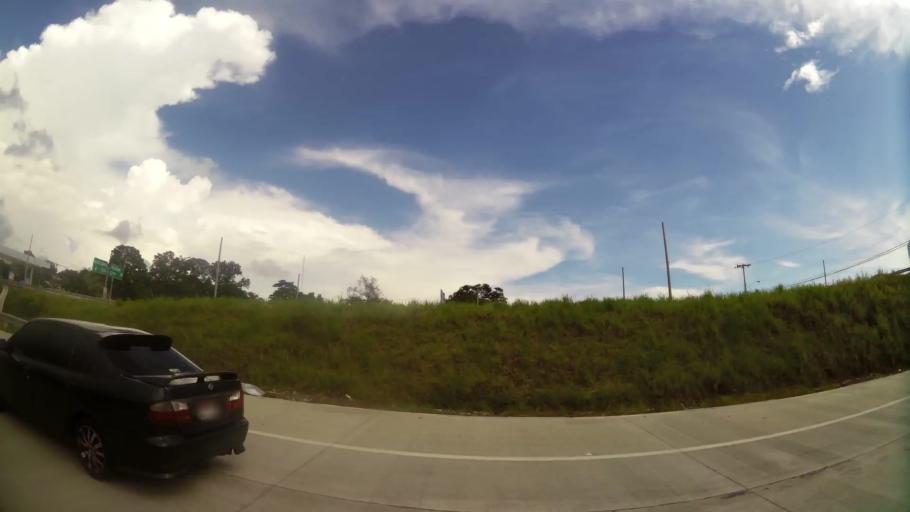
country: PA
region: Panama
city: San Miguelito
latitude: 9.0852
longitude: -79.4436
